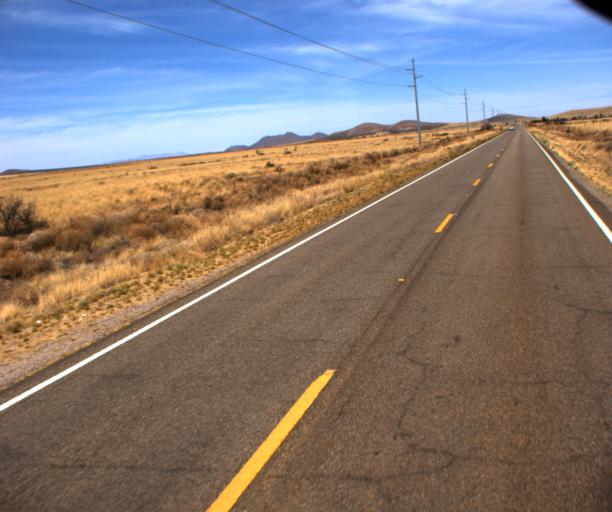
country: US
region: Arizona
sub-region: Cochise County
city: Tombstone
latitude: 31.8620
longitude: -109.6951
